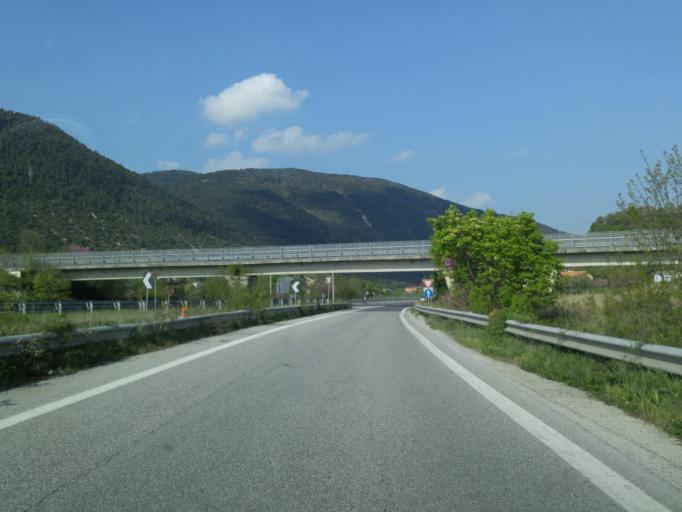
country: IT
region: The Marches
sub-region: Provincia di Pesaro e Urbino
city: Fossombrone
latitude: 43.6762
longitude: 12.7646
